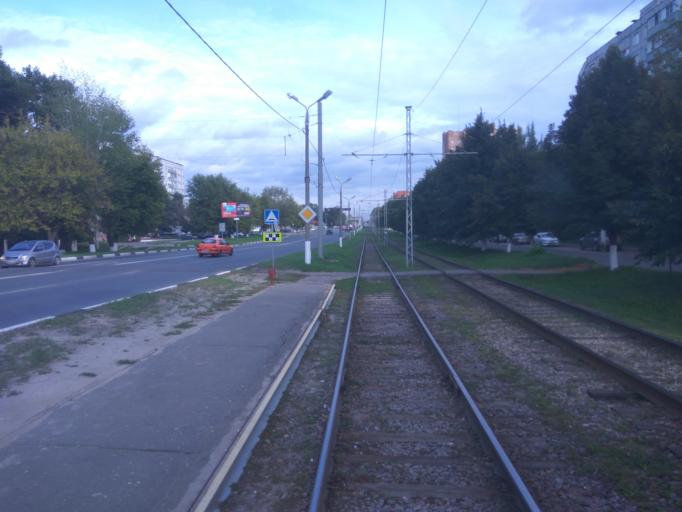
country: RU
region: Moskovskaya
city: Kolomna
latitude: 55.0874
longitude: 38.7913
